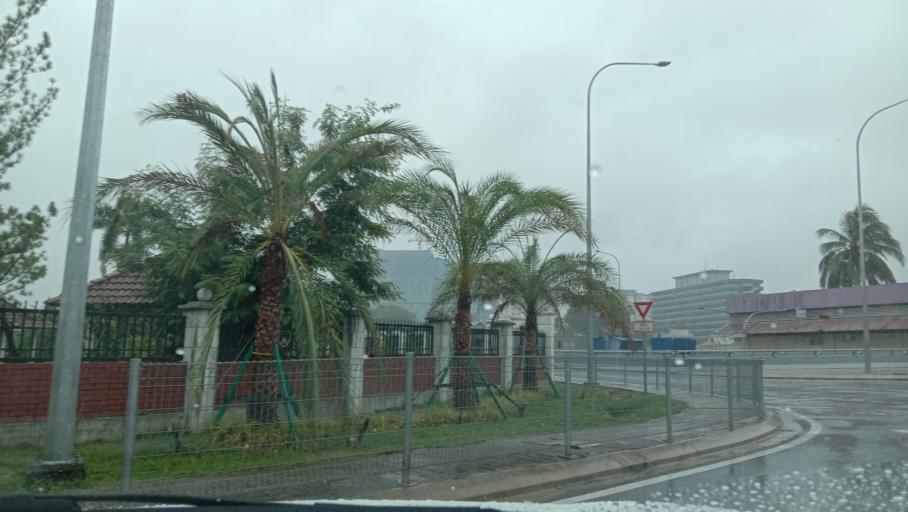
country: MY
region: Kuala Lumpur
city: Kuala Lumpur
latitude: 3.1756
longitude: 101.7200
